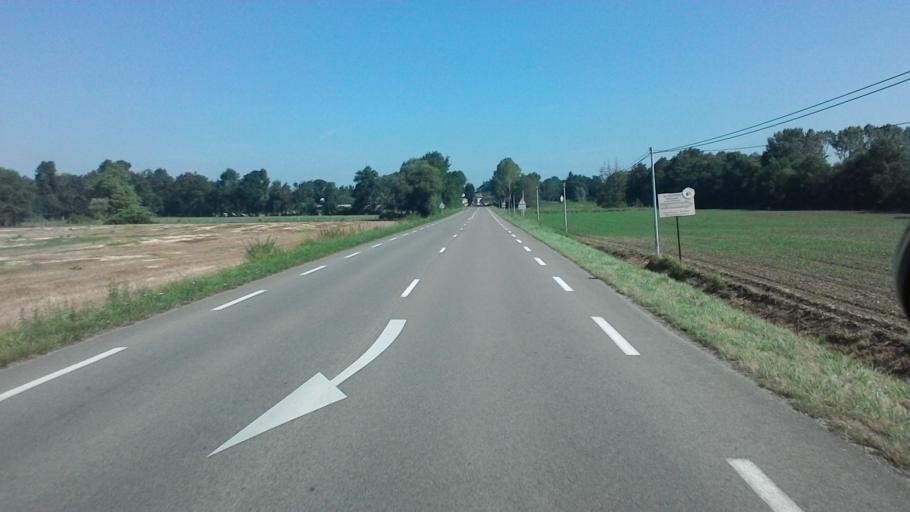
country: FR
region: Rhone-Alpes
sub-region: Departement de l'Ain
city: Montrevel-en-Bresse
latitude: 46.3947
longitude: 5.1145
